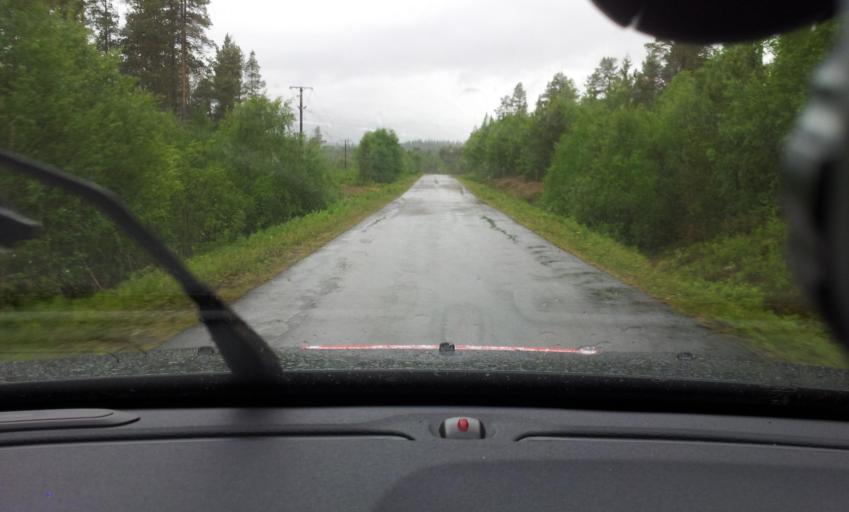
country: SE
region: Jaemtland
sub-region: Are Kommun
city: Are
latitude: 63.1481
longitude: 12.9448
